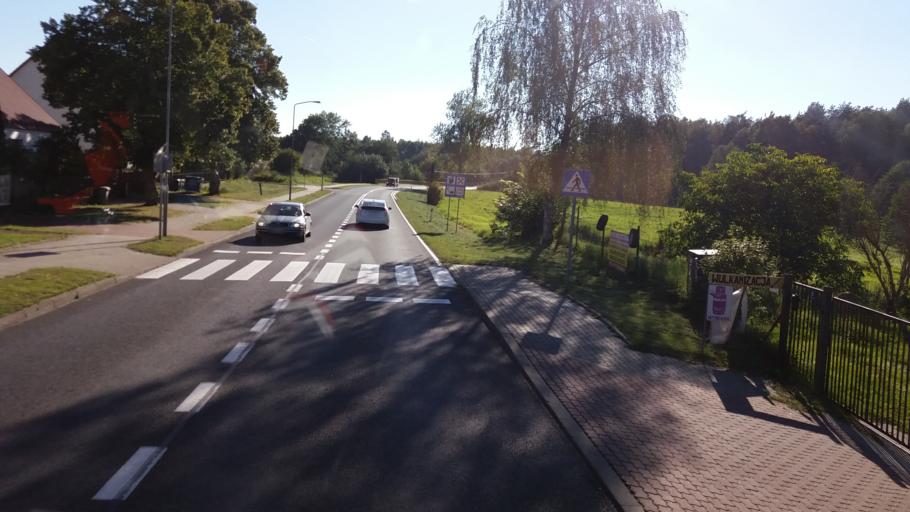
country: PL
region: West Pomeranian Voivodeship
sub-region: Powiat drawski
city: Kalisz Pomorski
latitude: 53.2924
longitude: 15.8916
